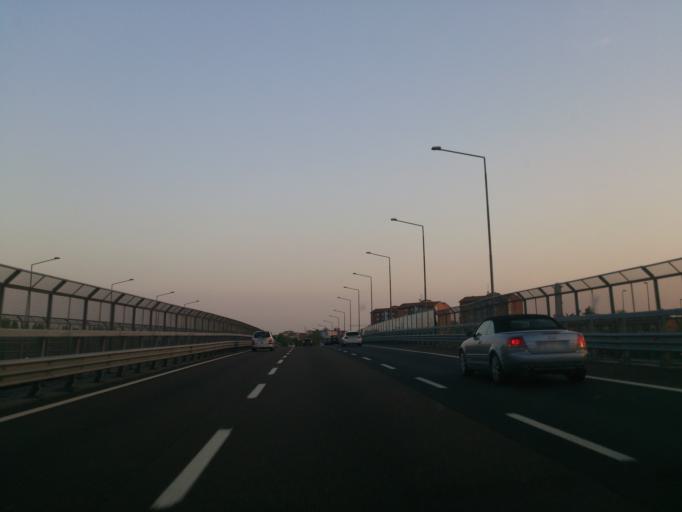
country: IT
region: Lombardy
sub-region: Citta metropolitana di Milano
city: Linate
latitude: 45.4619
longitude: 9.2510
